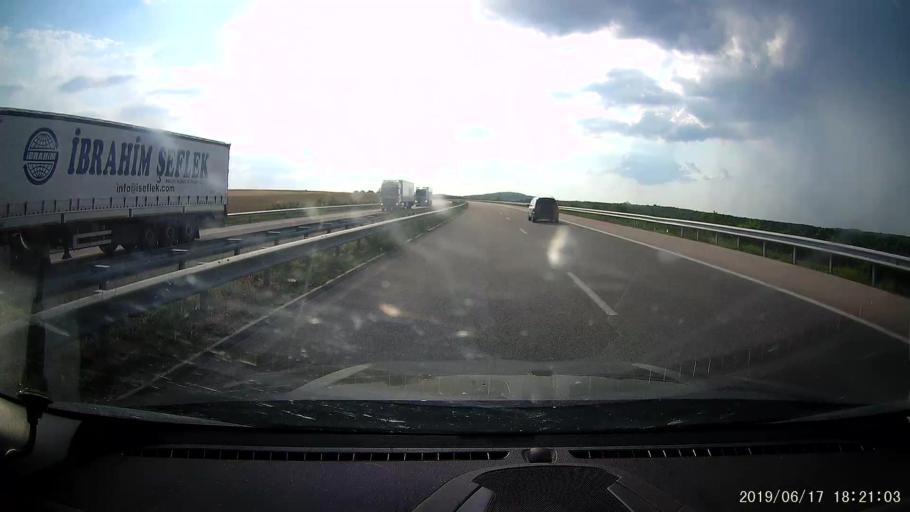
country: BG
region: Khaskovo
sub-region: Obshtina Simeonovgrad
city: Simeonovgrad
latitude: 41.9663
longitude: 25.7951
